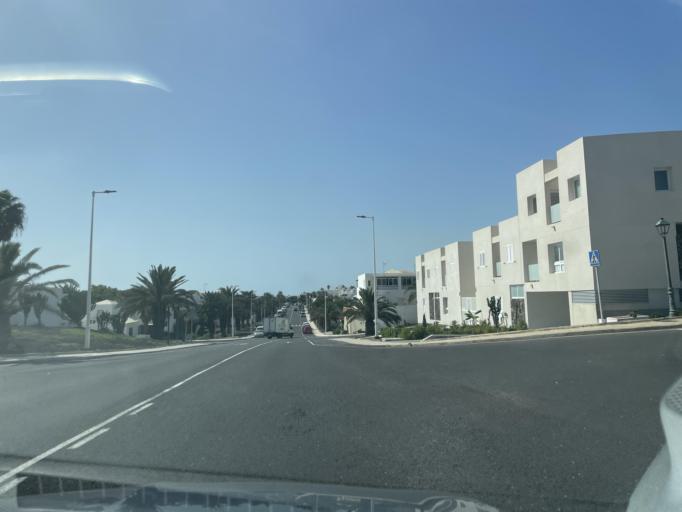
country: ES
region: Canary Islands
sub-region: Provincia de Las Palmas
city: Arrecife
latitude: 28.9970
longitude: -13.4966
